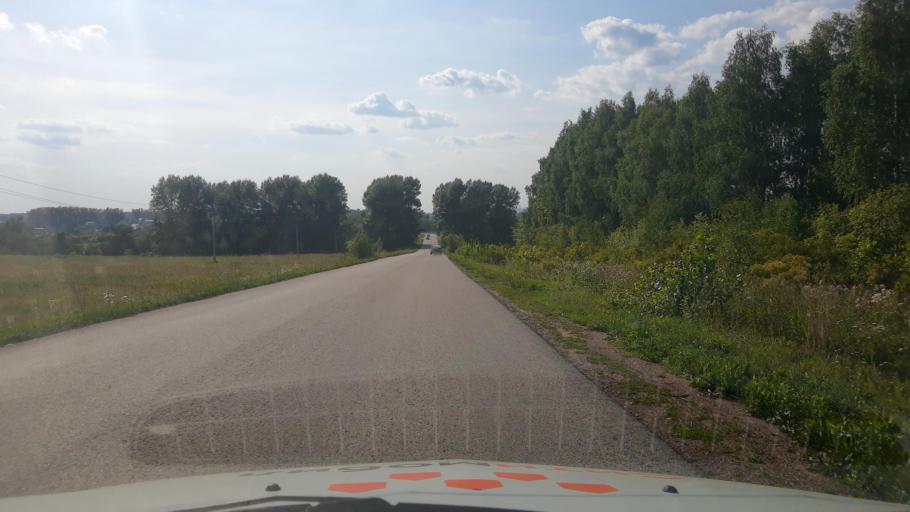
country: RU
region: Bashkortostan
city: Kabakovo
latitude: 54.6618
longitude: 56.1853
